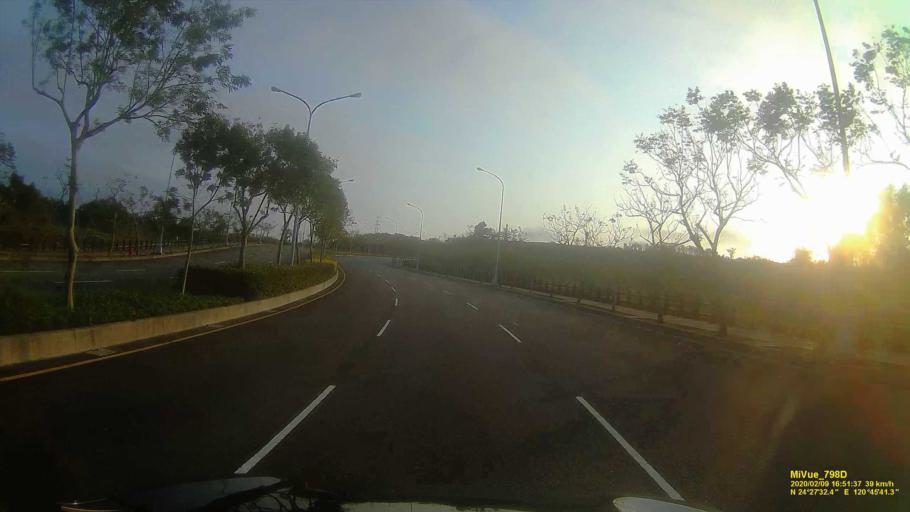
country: TW
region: Taiwan
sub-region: Miaoli
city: Miaoli
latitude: 24.4588
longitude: 120.7614
